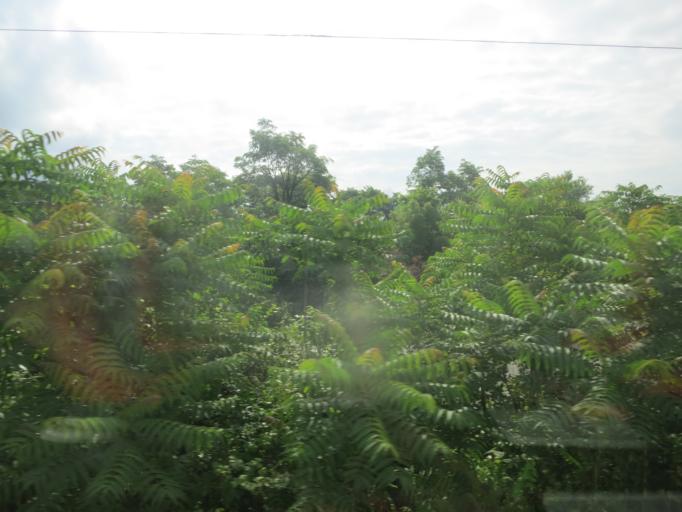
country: GE
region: Guria
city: Urek'i
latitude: 42.0364
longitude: 41.8126
